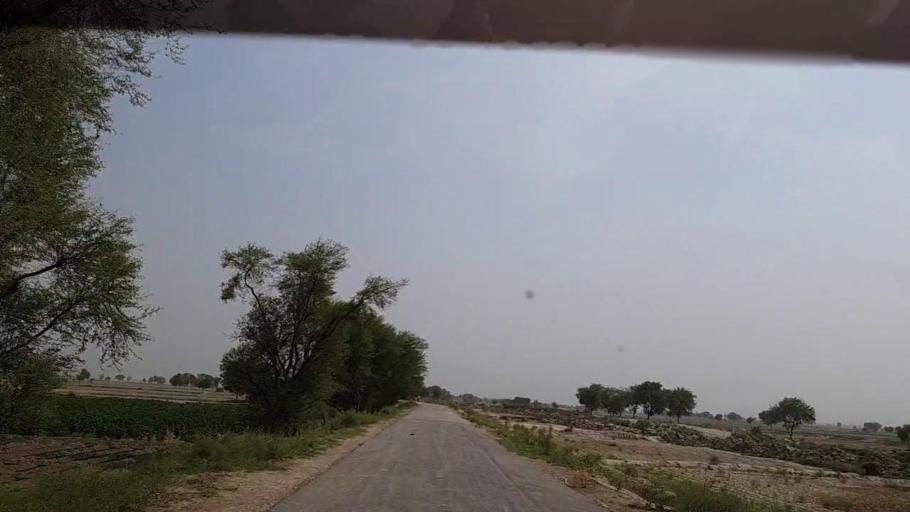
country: PK
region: Sindh
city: Khairpur Nathan Shah
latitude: 27.0738
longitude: 67.6880
